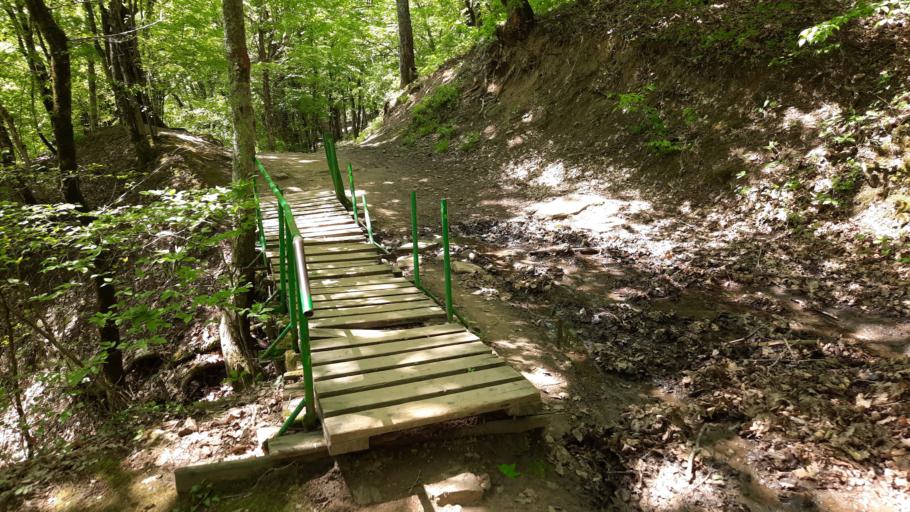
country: RU
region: Krasnodarskiy
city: Divnomorskoye
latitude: 44.5597
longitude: 38.2530
